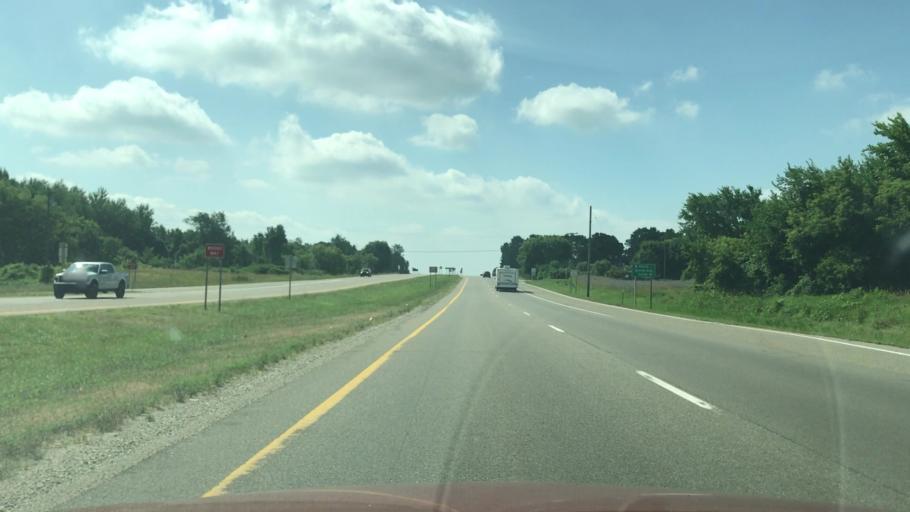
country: US
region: Michigan
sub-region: Kent County
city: Sparta
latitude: 43.1248
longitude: -85.7105
